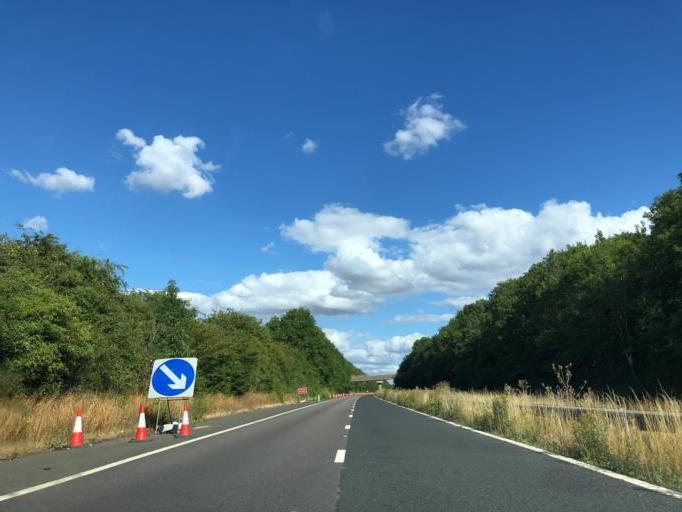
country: GB
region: England
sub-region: Warwickshire
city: Rugby
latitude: 52.3365
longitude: -1.2020
